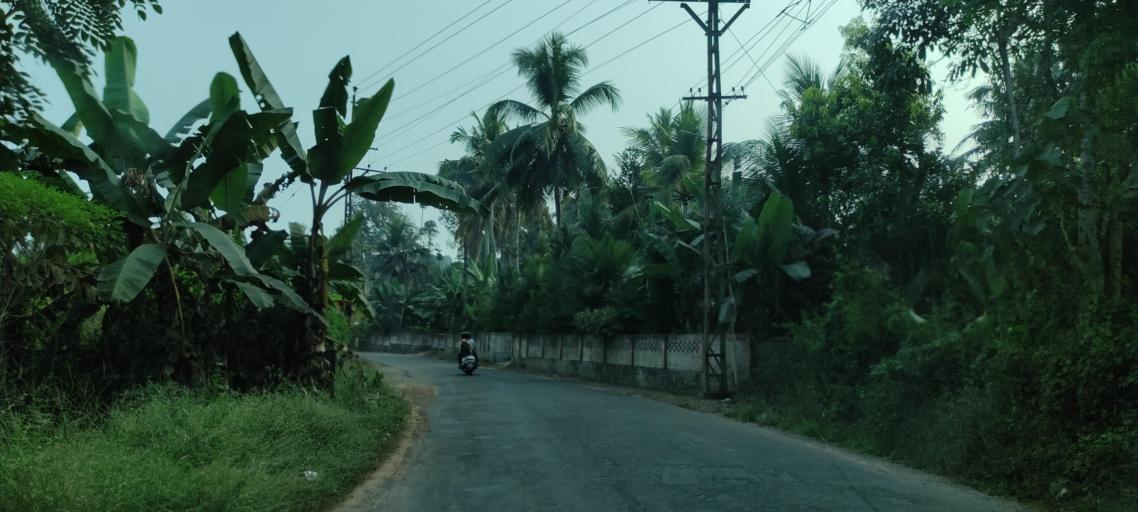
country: IN
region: Kerala
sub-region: Kottayam
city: Vaikam
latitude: 9.7249
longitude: 76.4766
